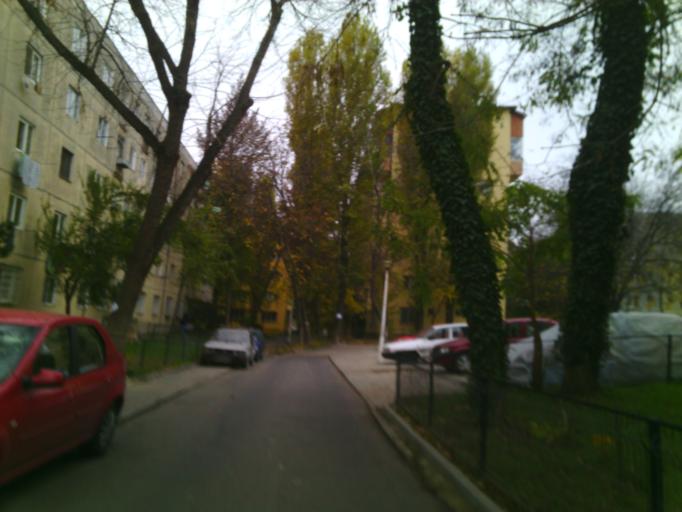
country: RO
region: Bucuresti
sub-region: Municipiul Bucuresti
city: Bucuresti
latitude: 44.3809
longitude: 26.0971
